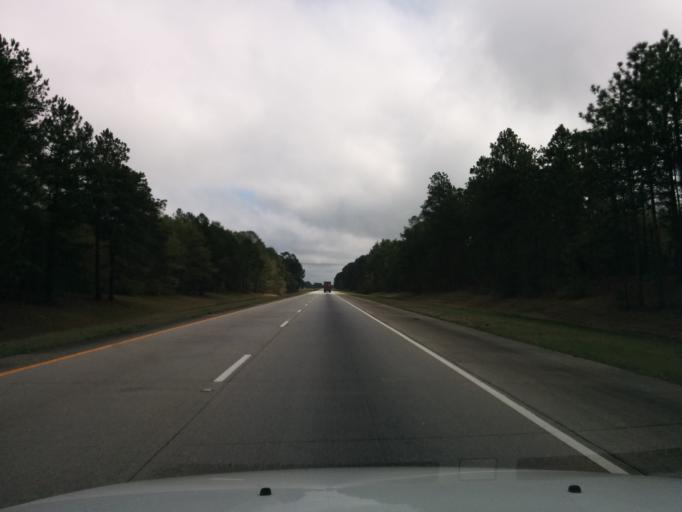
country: US
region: Georgia
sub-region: Treutlen County
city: Soperton
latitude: 32.4211
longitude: -82.4125
